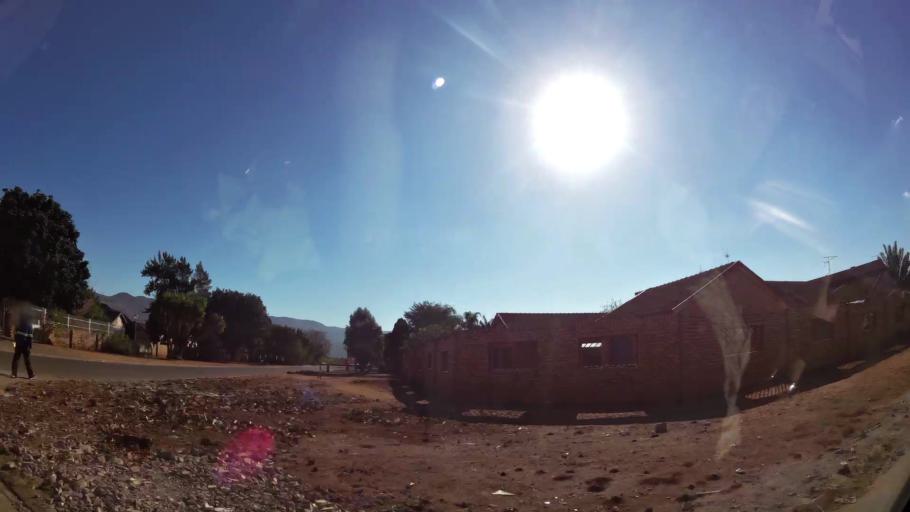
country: ZA
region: Limpopo
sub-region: Waterberg District Municipality
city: Mokopane
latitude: -24.1807
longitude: 28.9935
